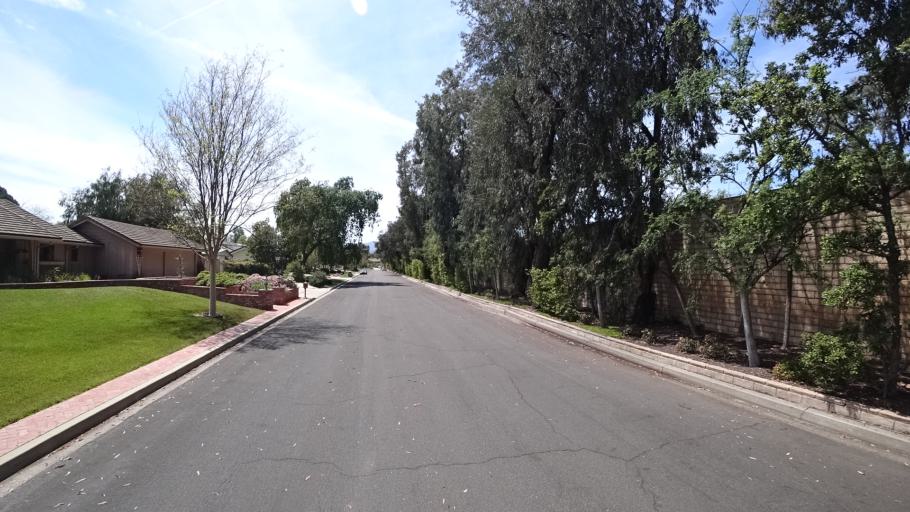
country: US
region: California
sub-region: Ventura County
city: Thousand Oaks
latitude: 34.1974
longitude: -118.8670
